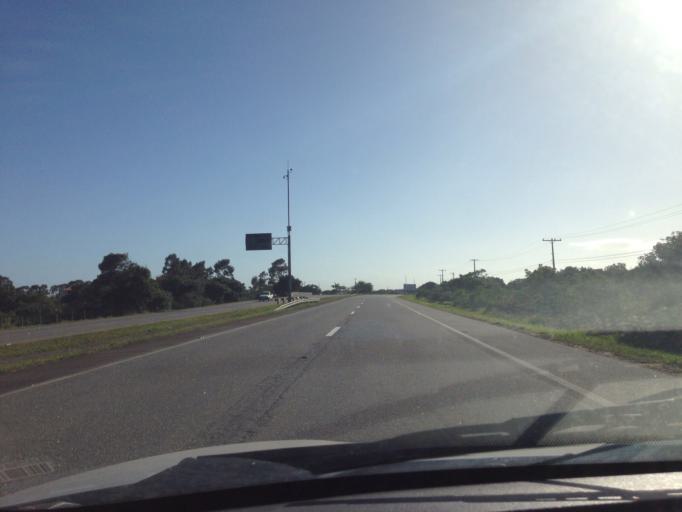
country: BR
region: Espirito Santo
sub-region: Guarapari
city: Guarapari
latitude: -20.5619
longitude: -40.4075
